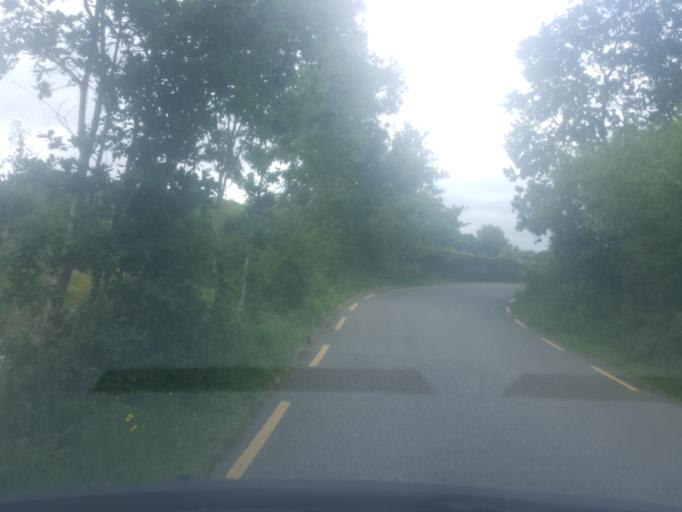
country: IE
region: Munster
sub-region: Ciarrai
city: Cill Airne
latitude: 52.0845
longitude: -9.4747
